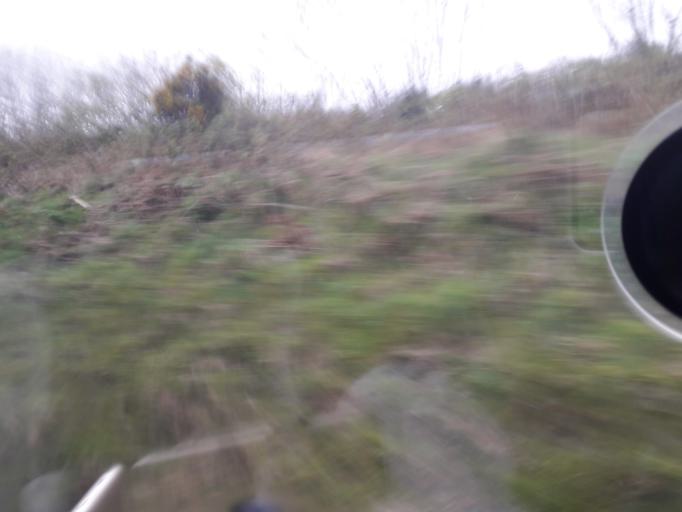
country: IE
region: Leinster
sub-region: An Iarmhi
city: An Muileann gCearr
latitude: 53.6107
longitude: -7.4060
